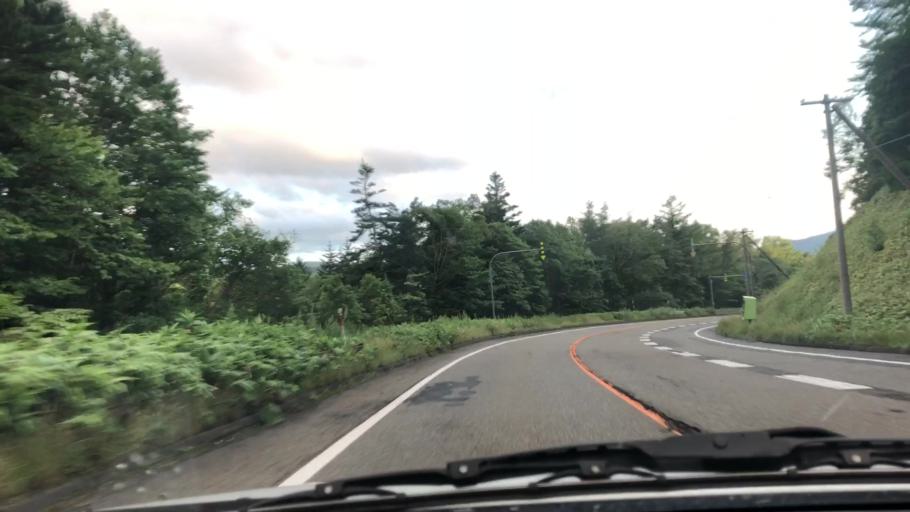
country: JP
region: Hokkaido
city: Shimo-furano
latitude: 42.8868
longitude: 142.2900
